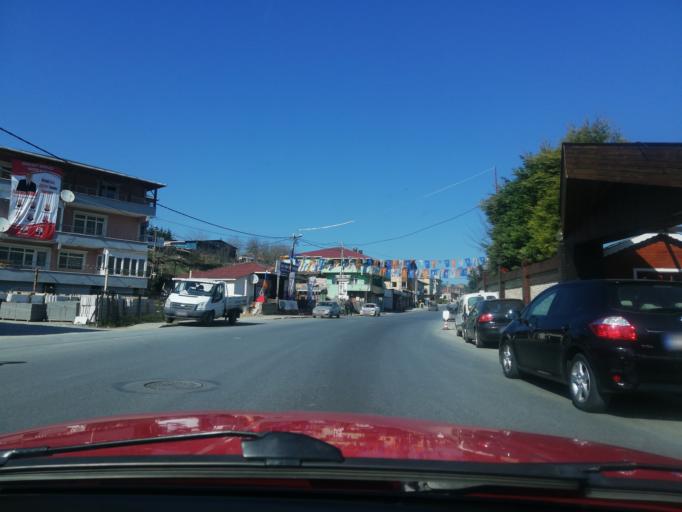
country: TR
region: Istanbul
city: Mahmut Sevket Pasa
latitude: 41.0924
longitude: 29.1420
